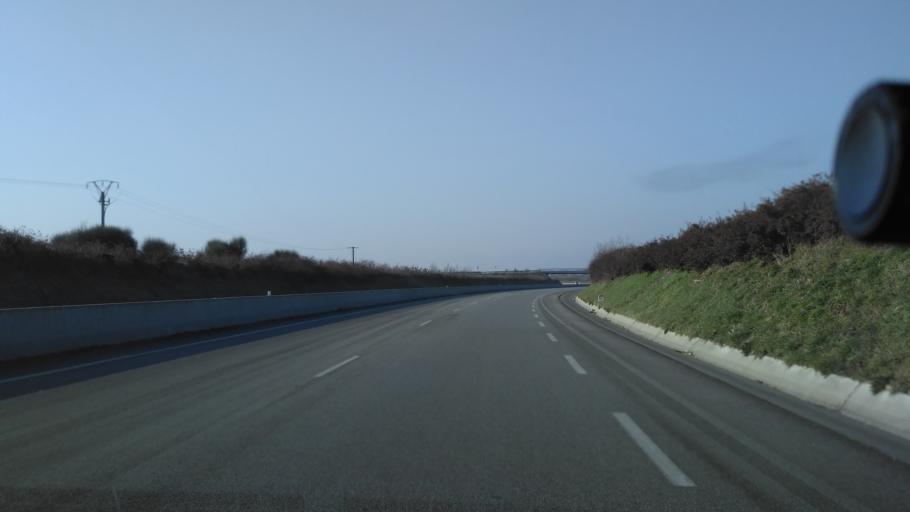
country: FR
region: Rhone-Alpes
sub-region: Departement de la Drome
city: Mours-Saint-Eusebe
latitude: 45.0602
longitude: 5.0334
